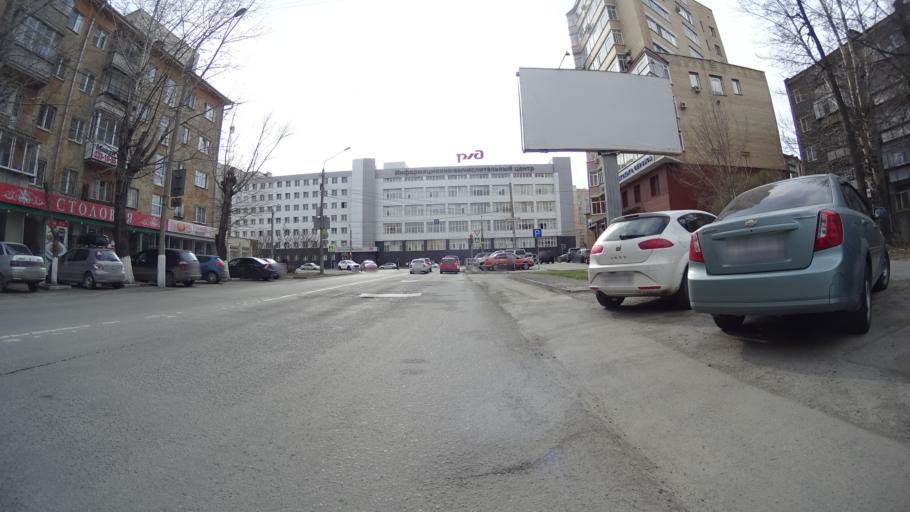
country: RU
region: Chelyabinsk
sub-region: Gorod Chelyabinsk
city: Chelyabinsk
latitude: 55.1501
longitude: 61.4128
